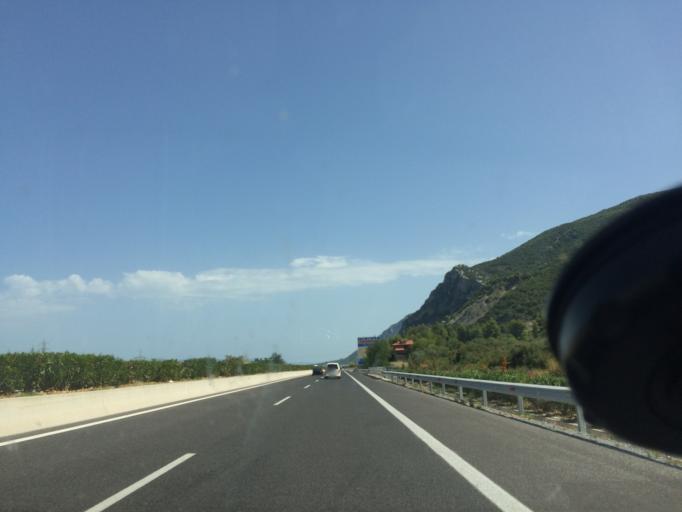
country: GR
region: Central Greece
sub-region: Nomos Fthiotidos
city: Kainouryion
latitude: 38.7792
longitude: 22.7286
